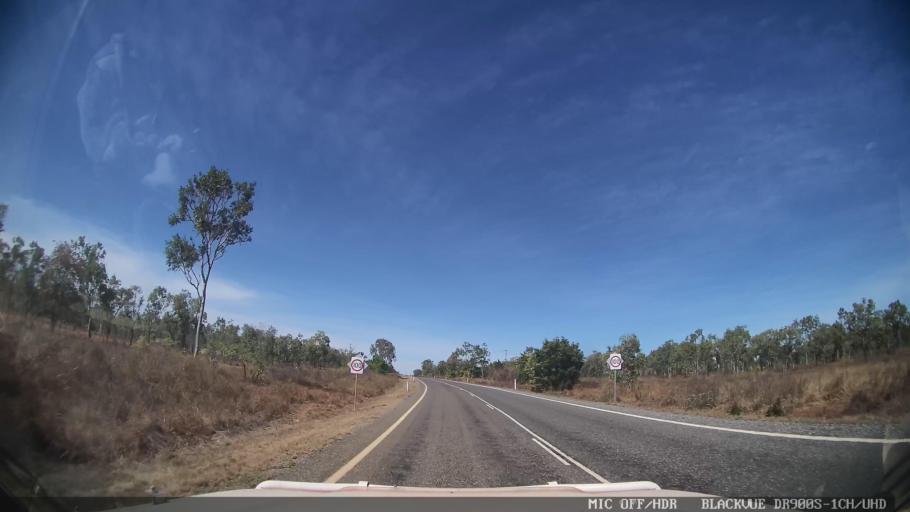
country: AU
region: Queensland
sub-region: Cook
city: Cooktown
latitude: -15.8656
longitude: 144.8073
